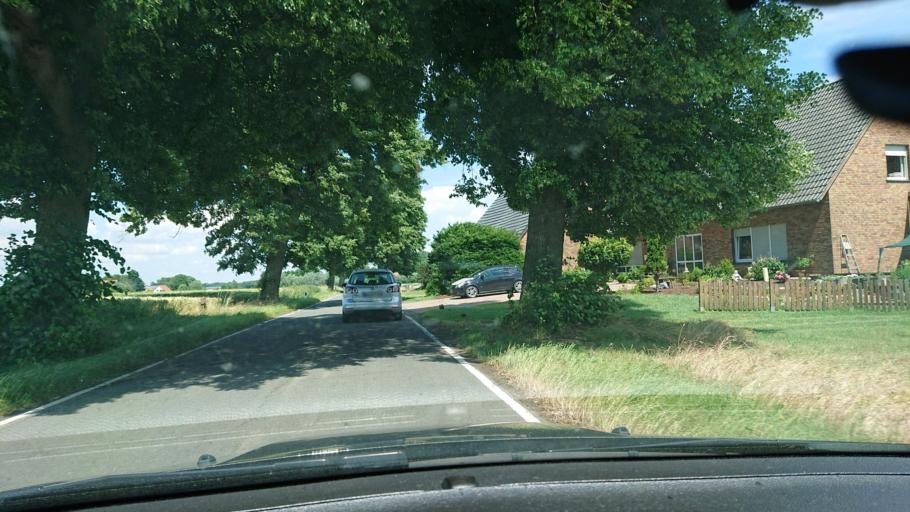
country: DE
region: North Rhine-Westphalia
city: Preussisch Oldendorf
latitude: 52.3245
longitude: 8.4728
